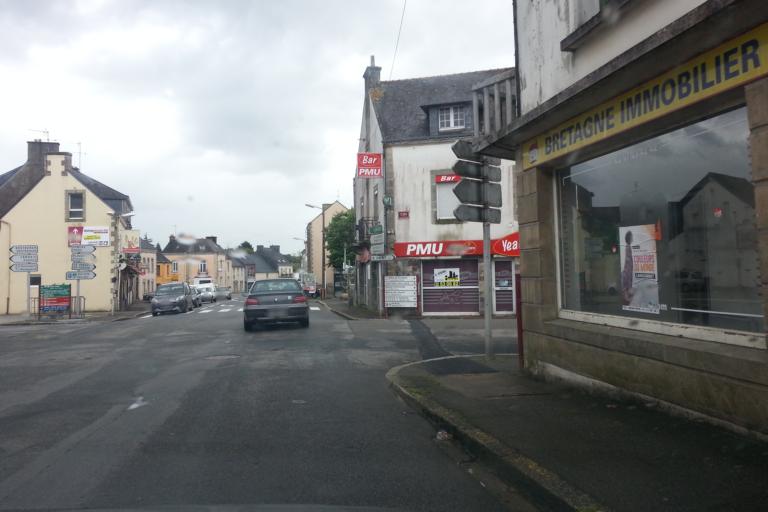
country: FR
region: Brittany
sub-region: Departement du Morbihan
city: Gourin
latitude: 48.1403
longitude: -3.6045
